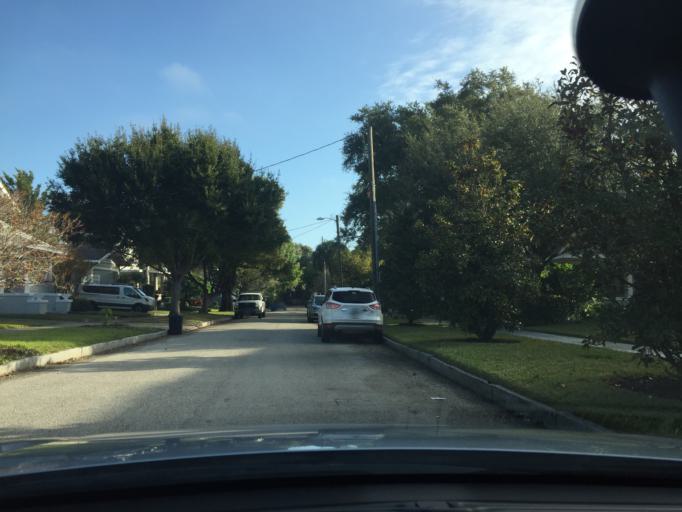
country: US
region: Florida
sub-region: Hillsborough County
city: Tampa
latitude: 27.9301
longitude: -82.4777
